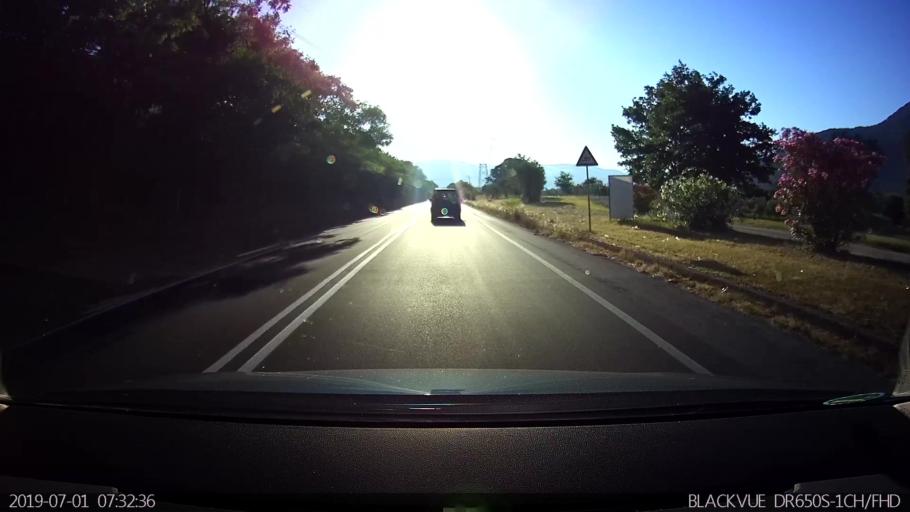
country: IT
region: Latium
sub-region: Provincia di Latina
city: Prossedi
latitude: 41.5068
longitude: 13.2487
